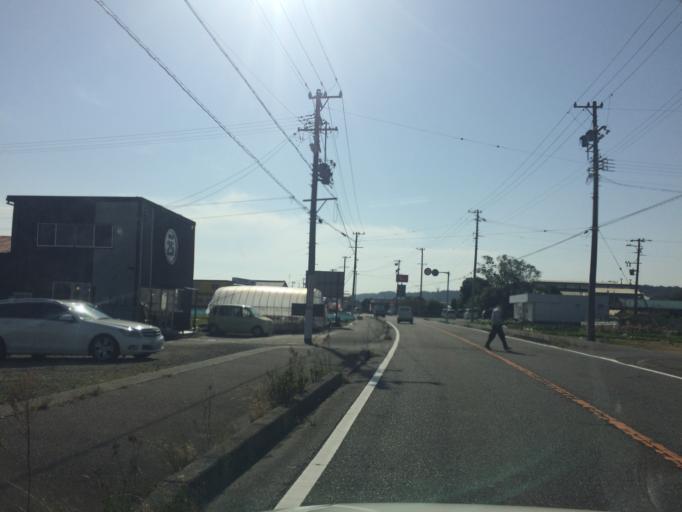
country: JP
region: Shizuoka
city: Sagara
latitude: 34.7259
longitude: 138.2202
